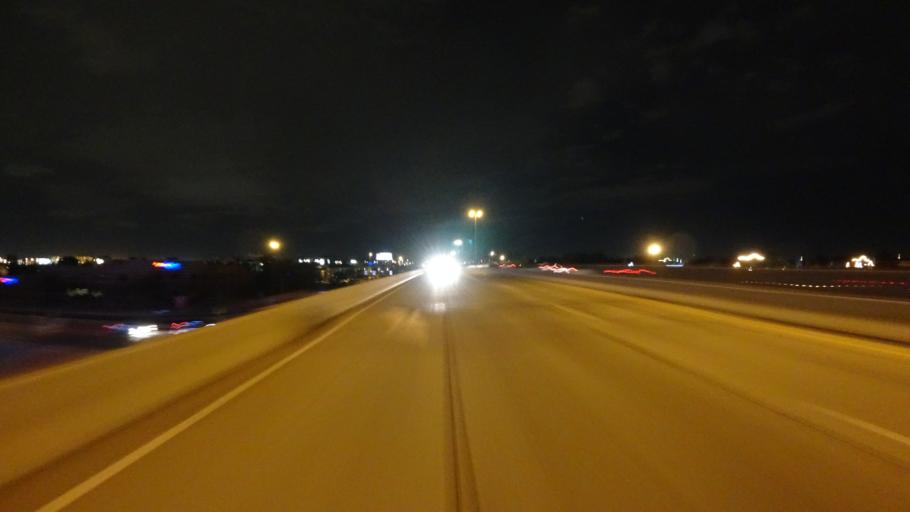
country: US
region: Arizona
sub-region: Maricopa County
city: Tempe Junction
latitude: 33.4215
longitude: -111.9782
